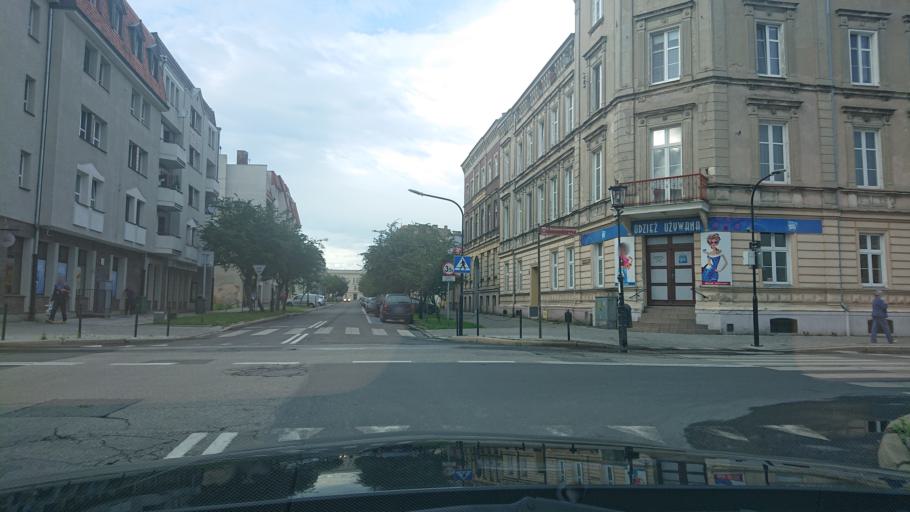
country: PL
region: Greater Poland Voivodeship
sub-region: Powiat gnieznienski
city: Gniezno
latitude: 52.5336
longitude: 17.6020
